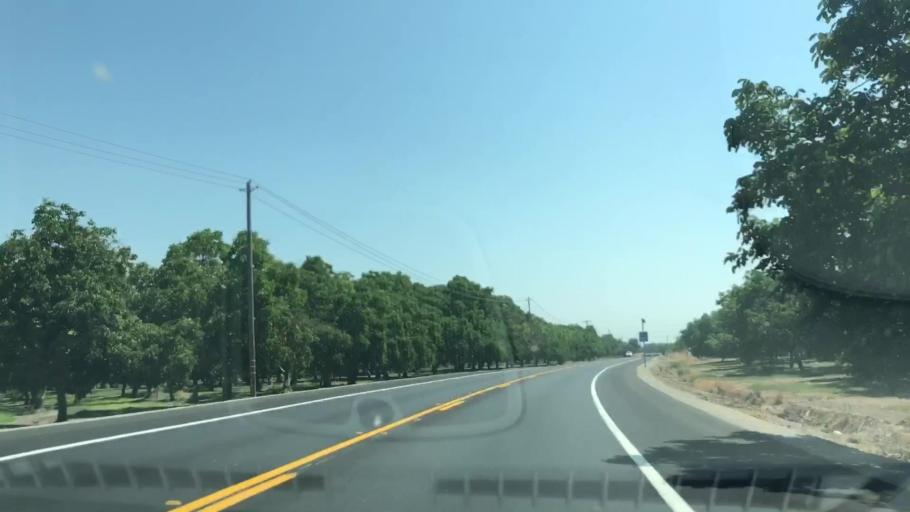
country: US
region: California
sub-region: San Joaquin County
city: Garden Acres
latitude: 37.9482
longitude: -121.1618
